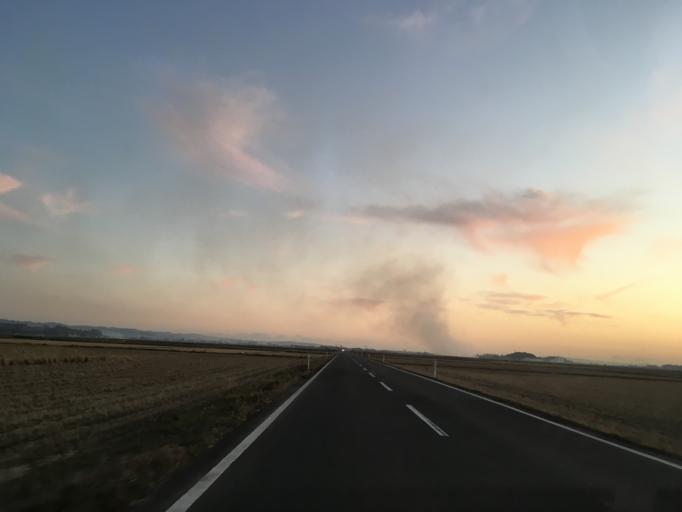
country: JP
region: Iwate
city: Ichinoseki
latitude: 38.7541
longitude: 141.2365
